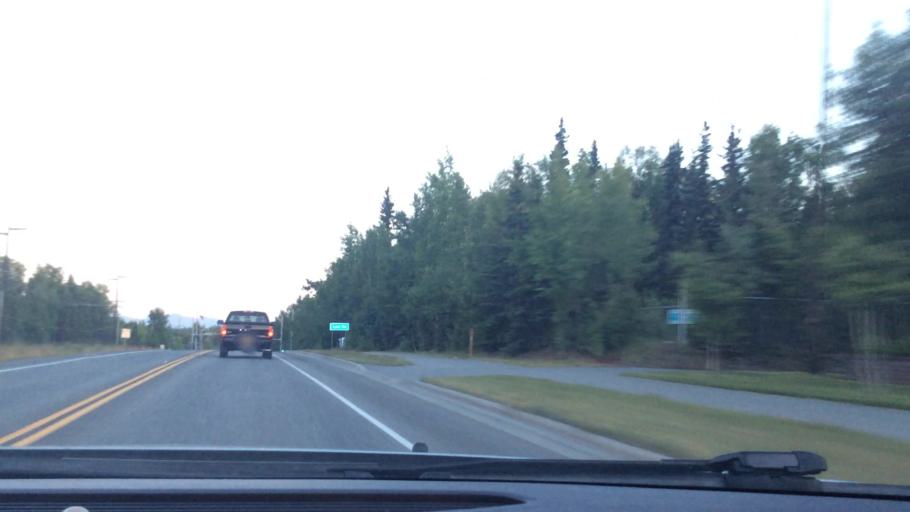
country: US
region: Alaska
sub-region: Anchorage Municipality
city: Anchorage
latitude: 61.1540
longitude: -149.8042
